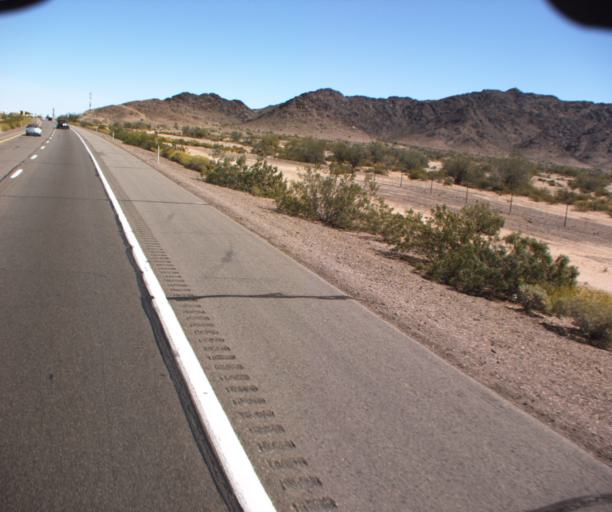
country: US
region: Arizona
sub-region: Yuma County
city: Wellton
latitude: 32.7230
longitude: -113.7598
